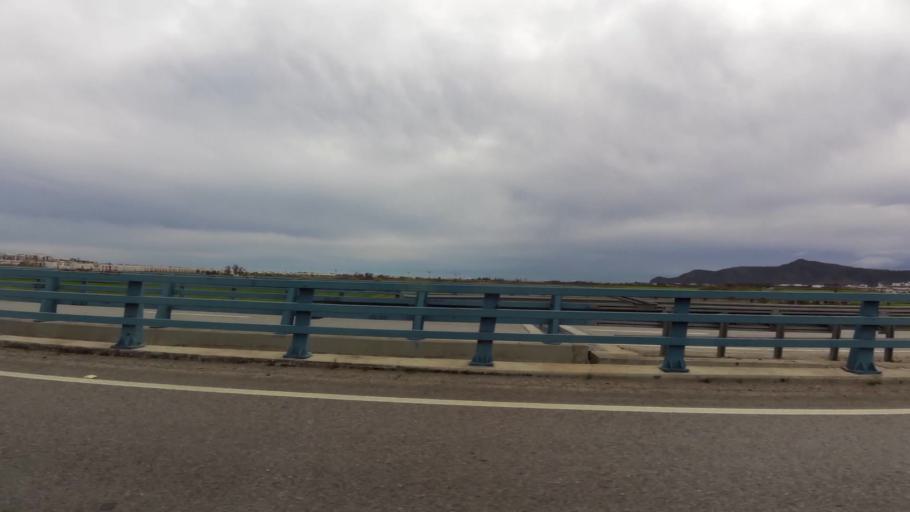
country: MA
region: Tanger-Tetouan
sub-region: Tetouan
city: Martil
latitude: 35.7096
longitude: -5.3560
